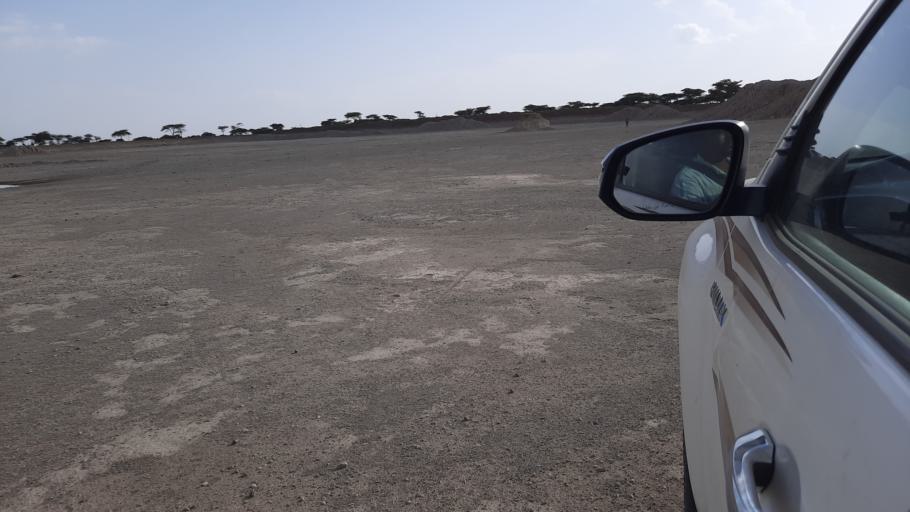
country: ET
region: Oromiya
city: Ziway
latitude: 7.6698
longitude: 38.6780
